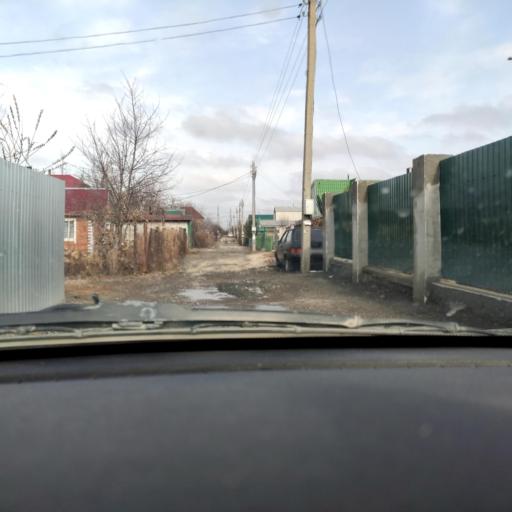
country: RU
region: Samara
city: Tol'yatti
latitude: 53.5850
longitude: 49.2902
